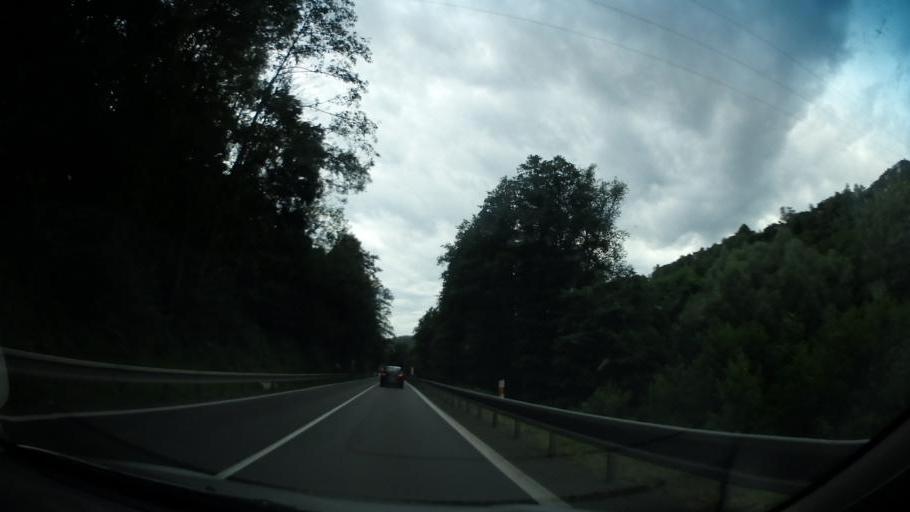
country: CZ
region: Pardubicky
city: Brnenec
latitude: 49.6067
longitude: 16.5314
